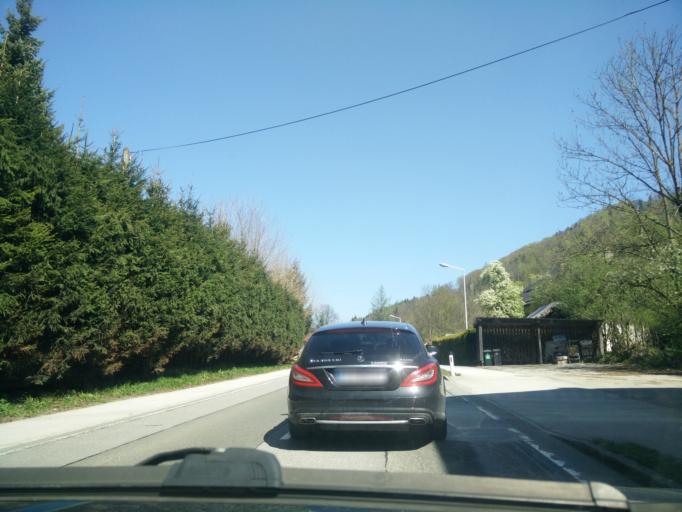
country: AT
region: Salzburg
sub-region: Politischer Bezirk Salzburg-Umgebung
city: Elsbethen
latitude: 47.7530
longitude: 13.0878
